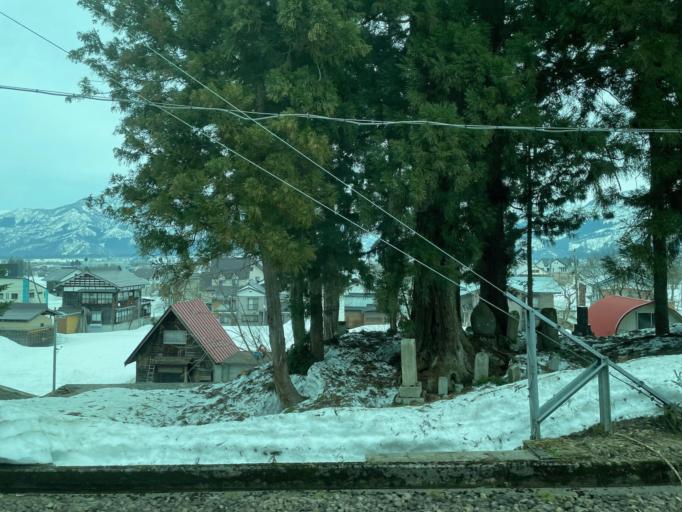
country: JP
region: Niigata
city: Shiozawa
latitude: 37.0220
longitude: 138.8217
